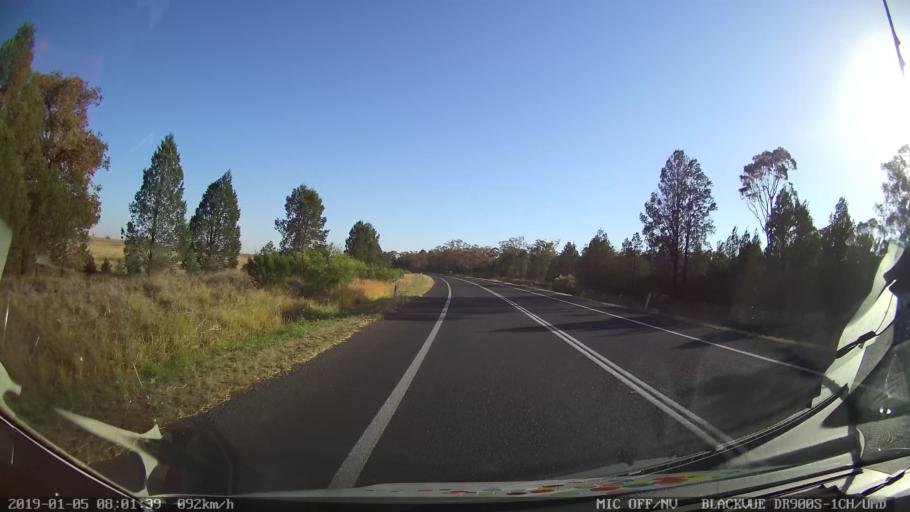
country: AU
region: New South Wales
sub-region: Gilgandra
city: Gilgandra
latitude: -31.6850
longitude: 148.7054
